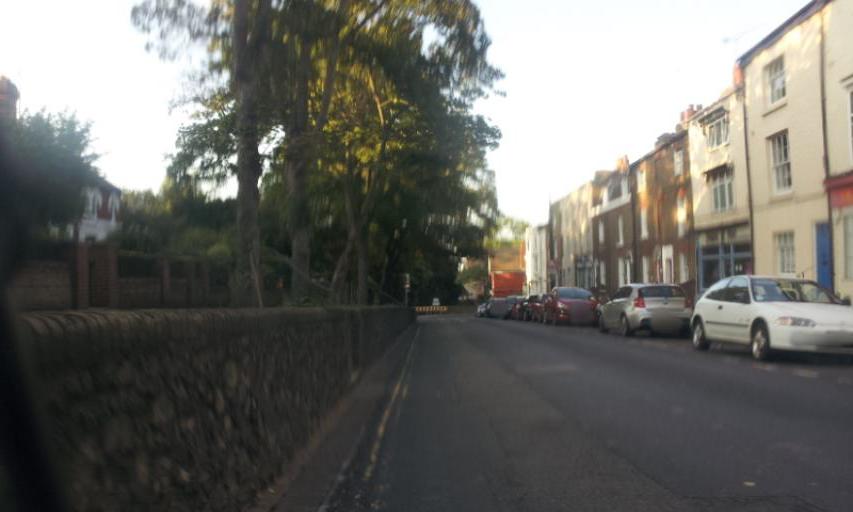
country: GB
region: England
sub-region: Medway
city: Rochester
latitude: 51.3845
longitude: 0.5035
